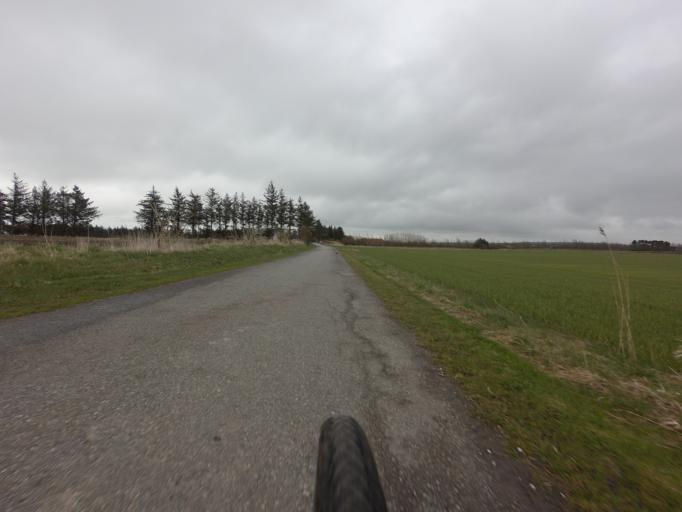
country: DK
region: North Denmark
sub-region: Jammerbugt Kommune
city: Pandrup
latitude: 57.3232
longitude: 9.7893
